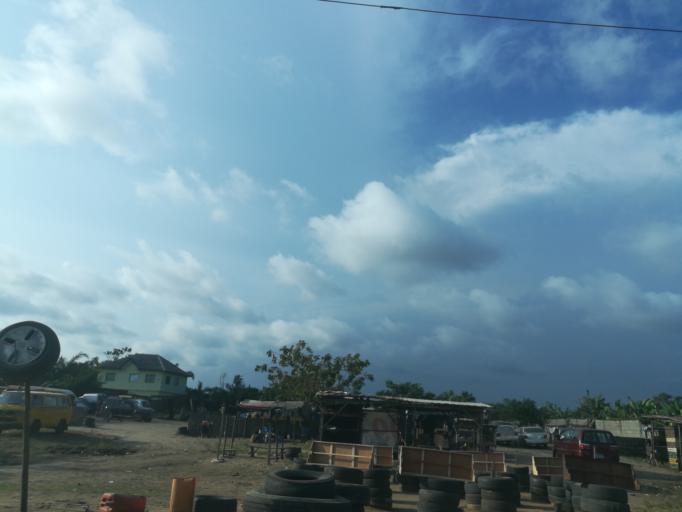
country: NG
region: Ogun
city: Ado Odo
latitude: 6.4835
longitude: 3.0427
